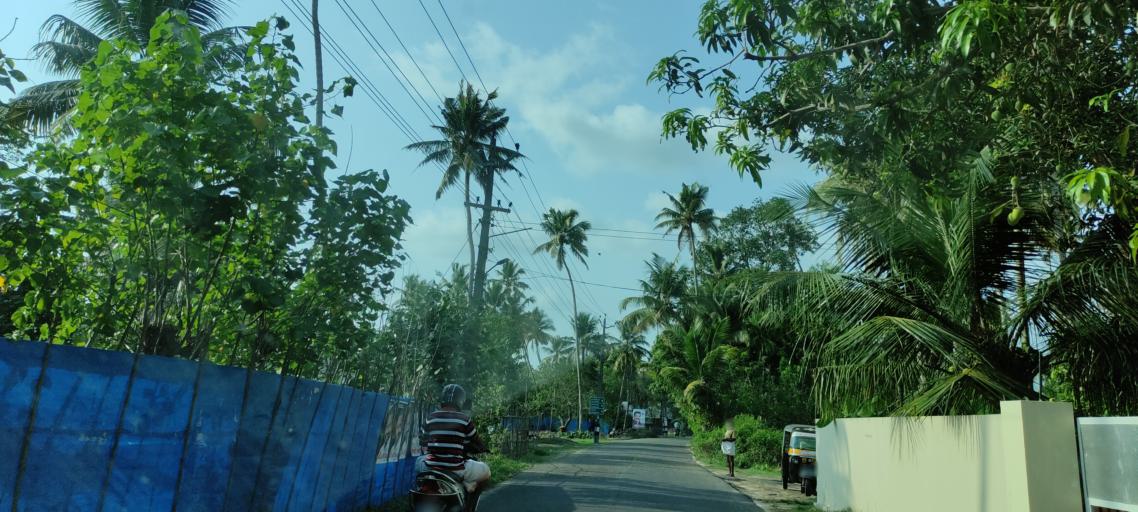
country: IN
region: Kerala
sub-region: Alappuzha
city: Vayalar
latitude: 9.6939
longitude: 76.2903
